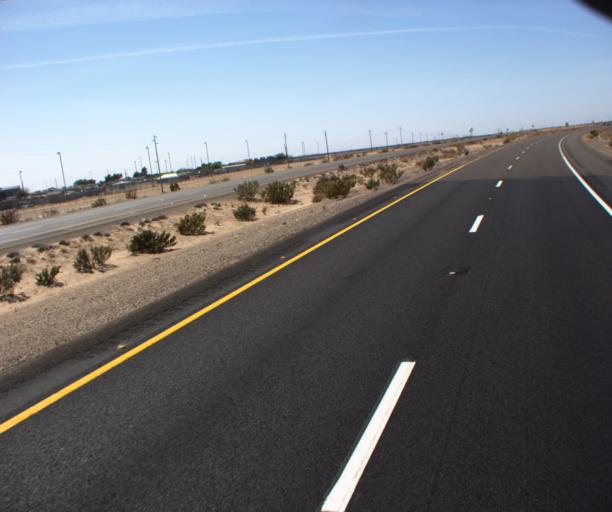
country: US
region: Arizona
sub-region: Yuma County
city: Somerton
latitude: 32.4954
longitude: -114.6391
